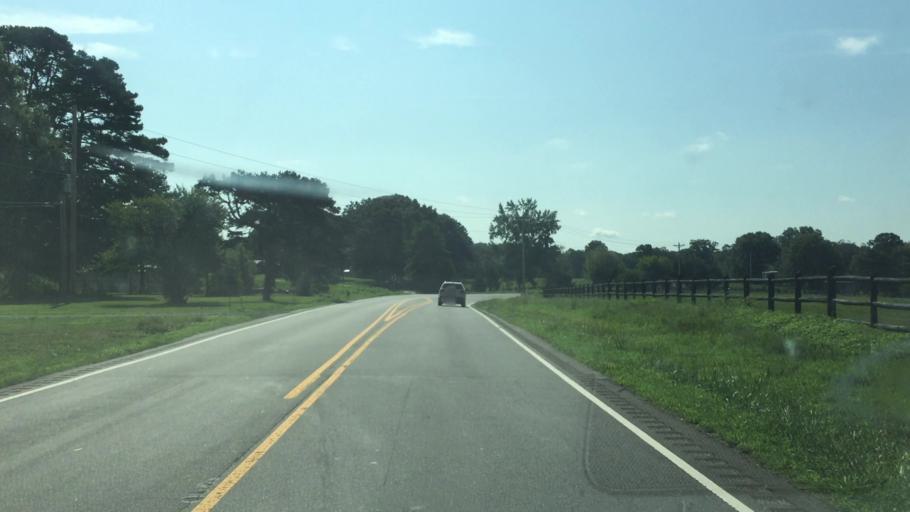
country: US
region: North Carolina
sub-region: Union County
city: Fairview
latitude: 35.1514
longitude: -80.5543
